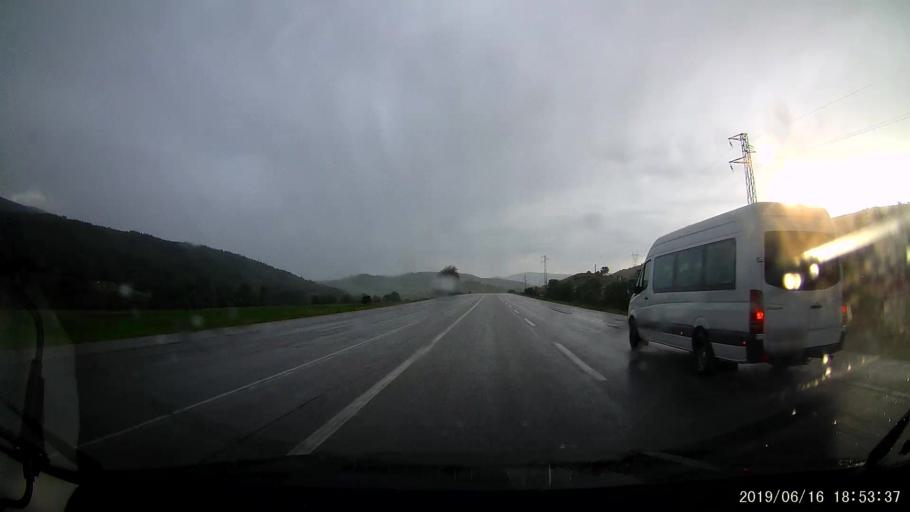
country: TR
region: Erzincan
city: Catalcam
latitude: 39.8977
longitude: 38.8732
